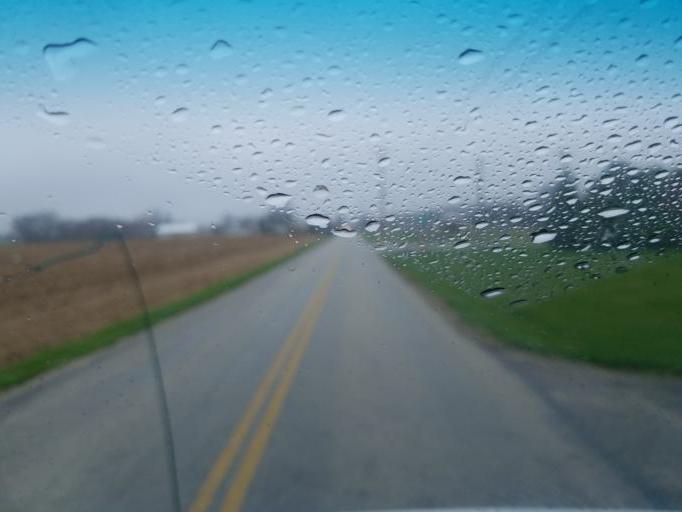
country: US
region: Ohio
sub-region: Wood County
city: North Baltimore
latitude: 41.1489
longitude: -83.6313
